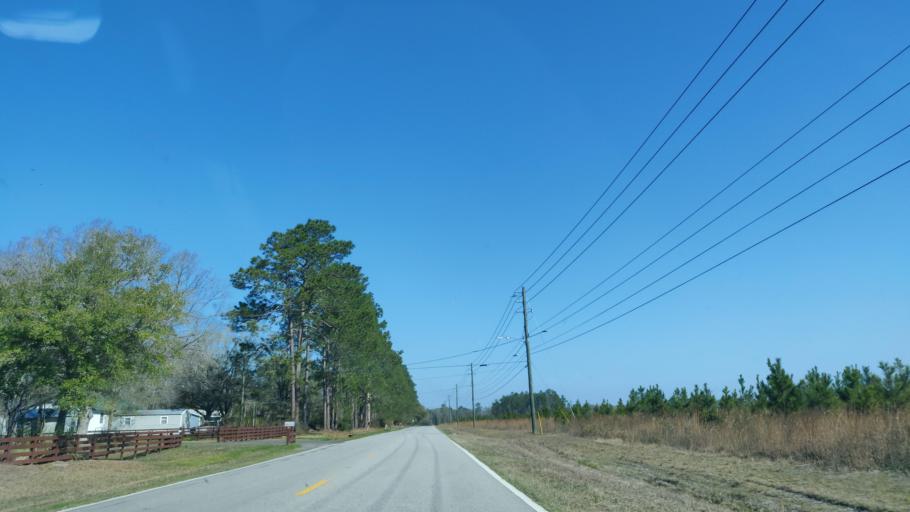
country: US
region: Florida
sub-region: Duval County
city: Baldwin
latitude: 30.2326
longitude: -81.9412
